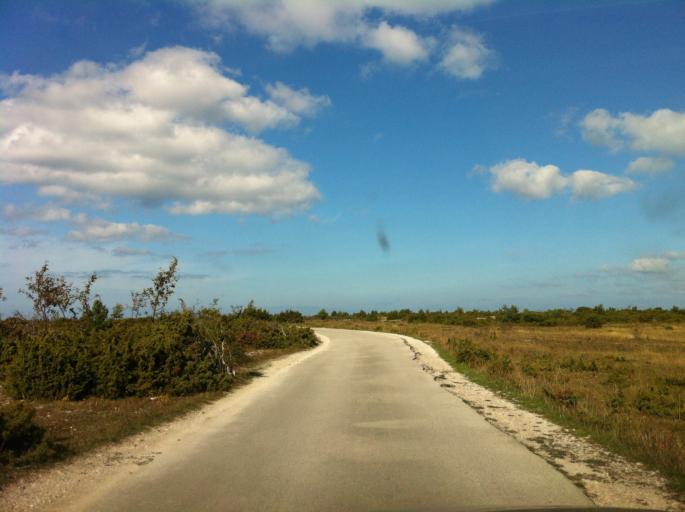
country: SE
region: Gotland
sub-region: Gotland
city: Slite
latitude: 57.9881
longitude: 19.1672
